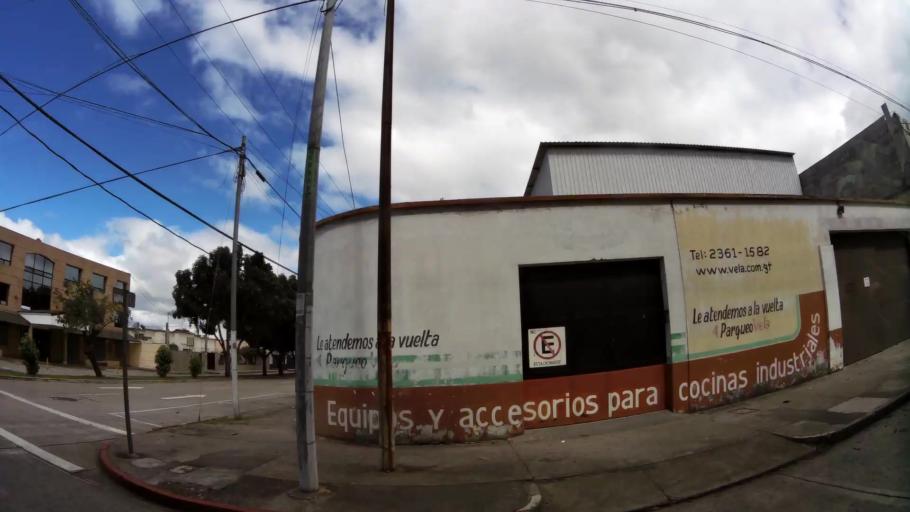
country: GT
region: Guatemala
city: Santa Catarina Pinula
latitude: 14.5989
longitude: -90.5223
